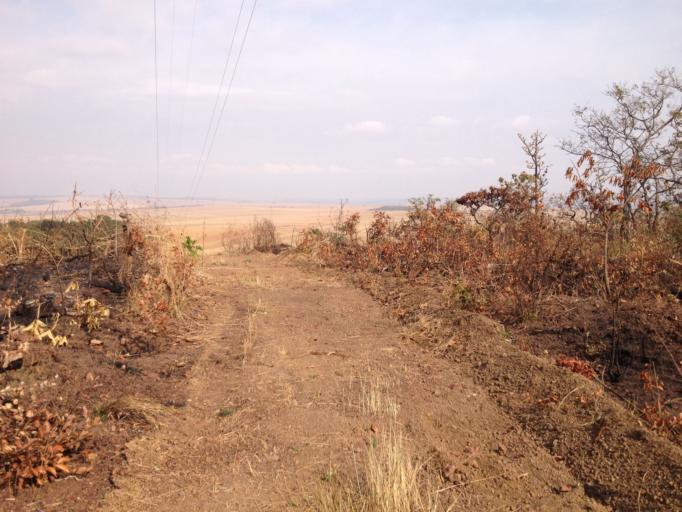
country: BR
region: Minas Gerais
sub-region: Paracatu
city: Paracatu
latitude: -17.3684
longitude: -47.3621
